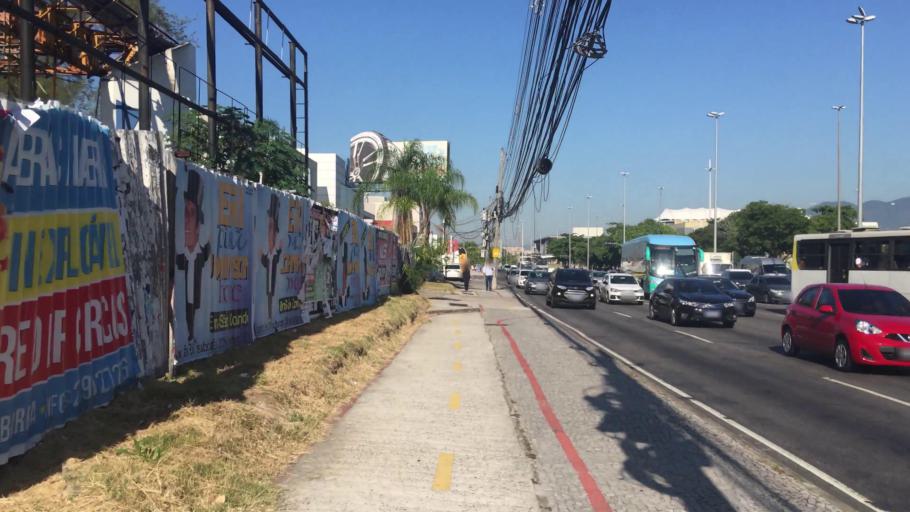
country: BR
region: Rio de Janeiro
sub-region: Rio De Janeiro
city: Rio de Janeiro
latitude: -23.0004
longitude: -43.3553
